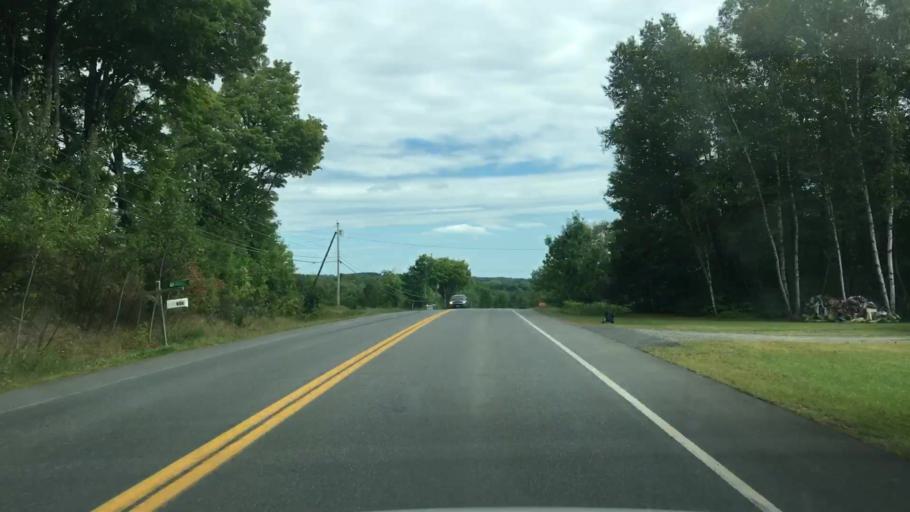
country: US
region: Maine
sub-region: Piscataquis County
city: Dover-Foxcroft
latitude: 45.2250
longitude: -69.1246
